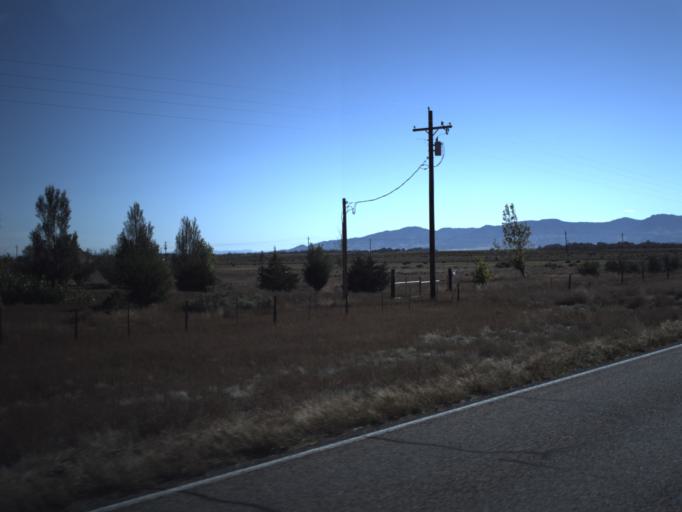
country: US
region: Utah
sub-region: Washington County
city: Enterprise
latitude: 37.7243
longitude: -113.6974
